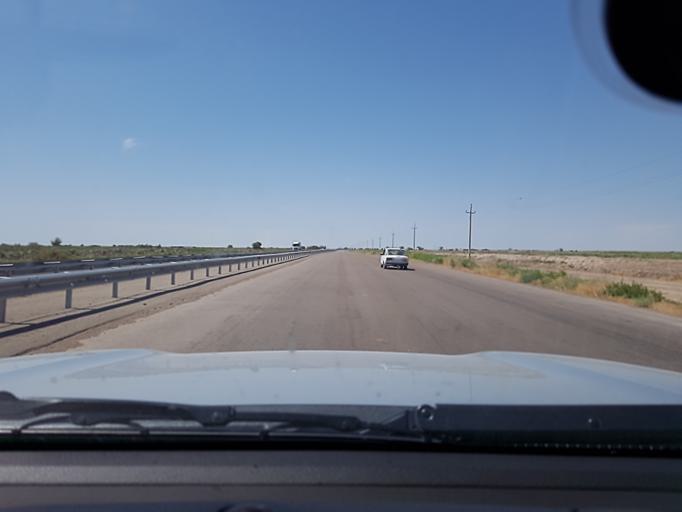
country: TM
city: Akdepe
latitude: 41.7366
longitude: 59.1157
